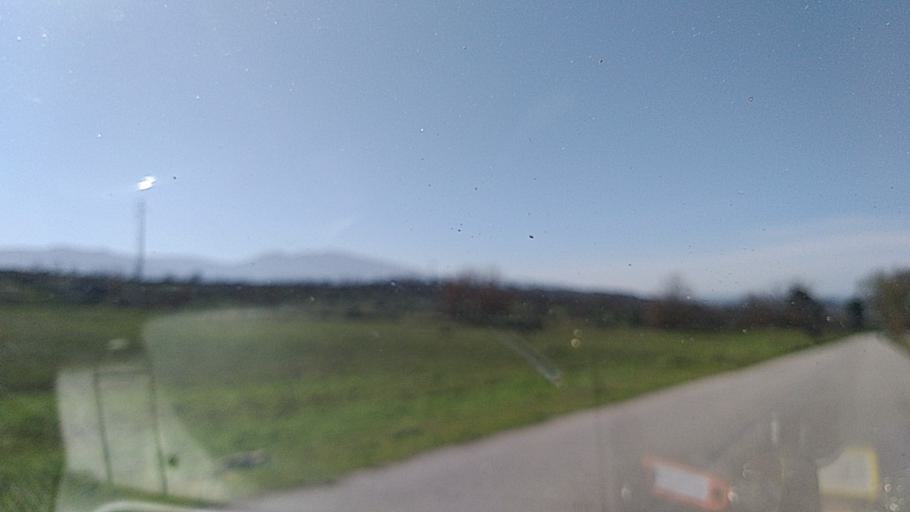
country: PT
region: Guarda
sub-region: Fornos de Algodres
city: Fornos de Algodres
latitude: 40.5913
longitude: -7.4751
